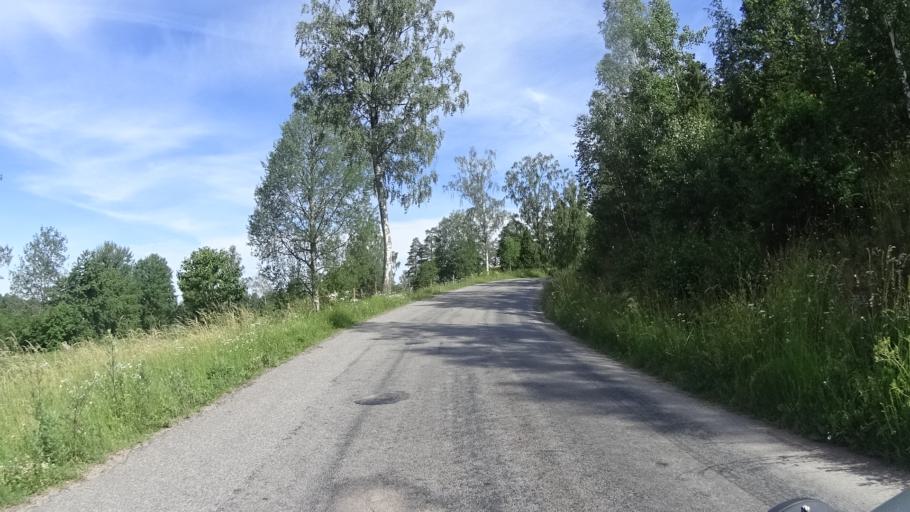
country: SE
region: Kalmar
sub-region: Vasterviks Kommun
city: Overum
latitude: 57.8764
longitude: 16.1749
